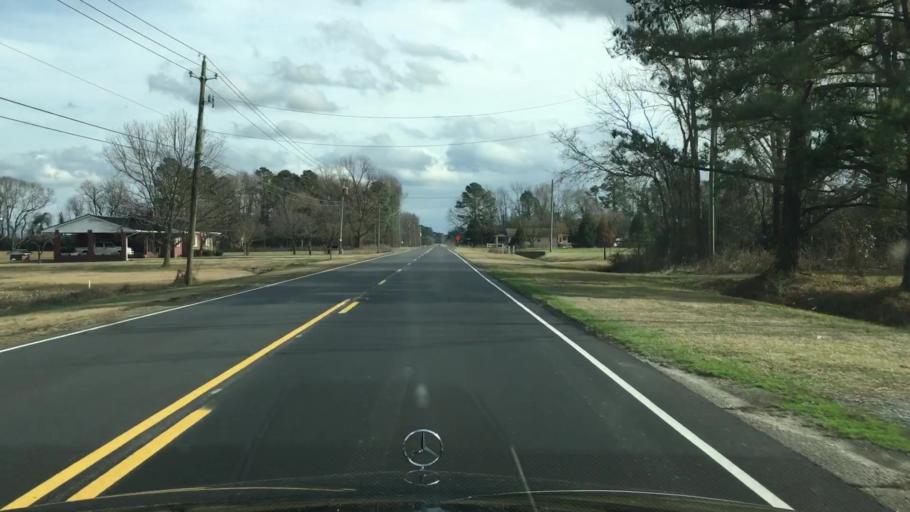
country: US
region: North Carolina
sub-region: Duplin County
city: Warsaw
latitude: 34.9819
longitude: -78.0350
